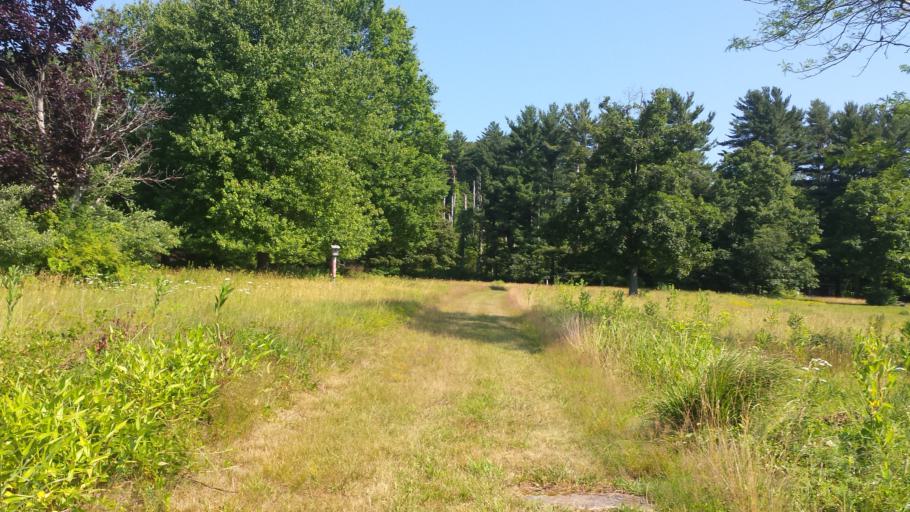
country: US
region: New York
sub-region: Westchester County
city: Pound Ridge
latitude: 41.2618
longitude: -73.6025
